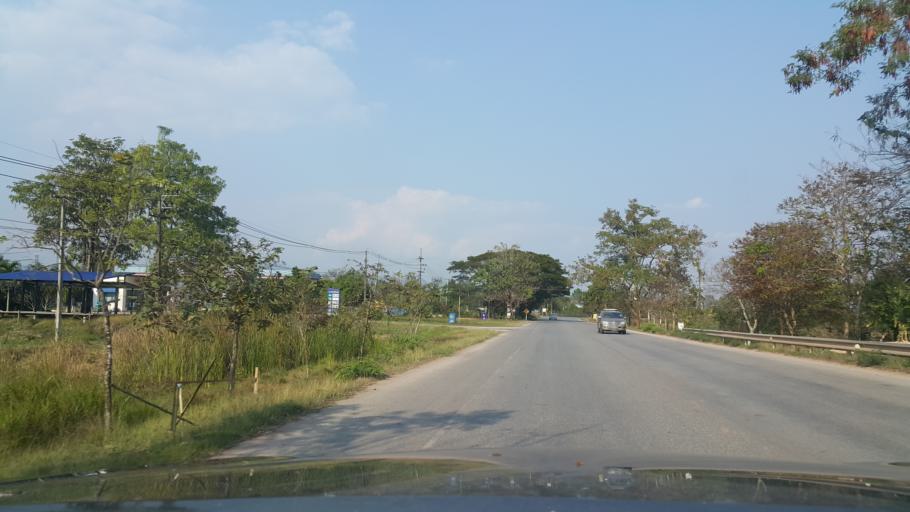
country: TH
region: Phitsanulok
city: Nakhon Thai
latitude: 17.0742
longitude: 100.8138
